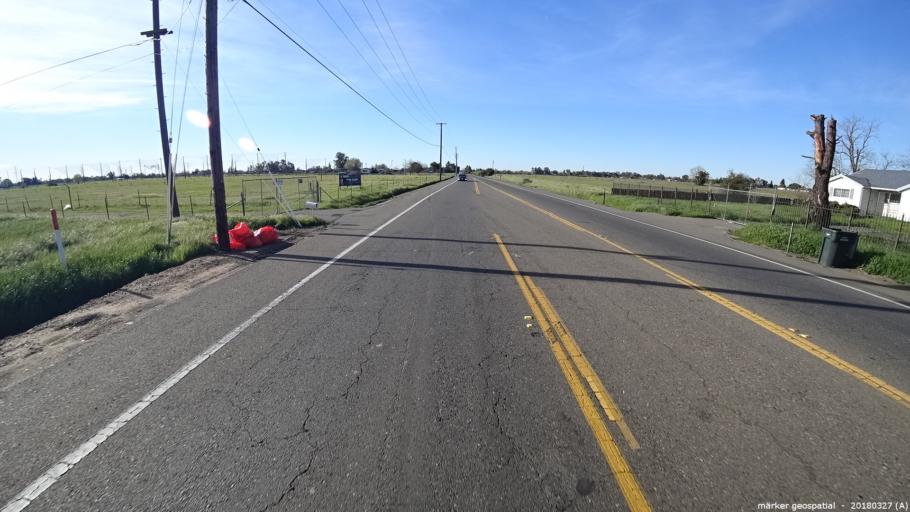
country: US
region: California
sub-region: Sacramento County
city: Florin
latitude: 38.4941
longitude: -121.3719
